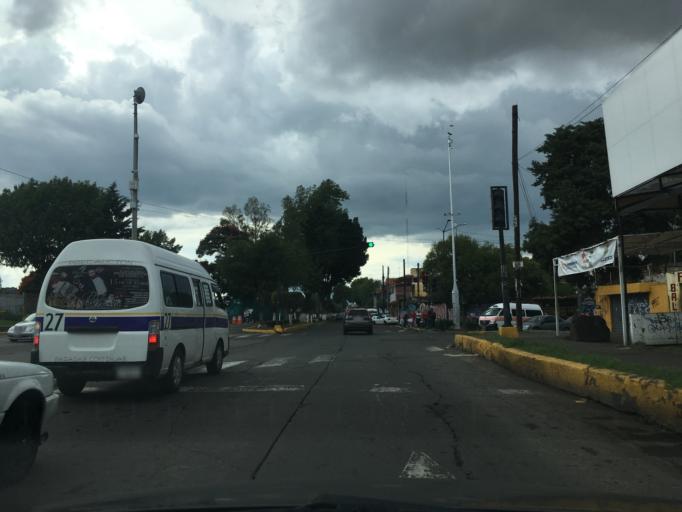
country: MX
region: Michoacan
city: Morelia
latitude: 19.7060
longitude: -101.2002
